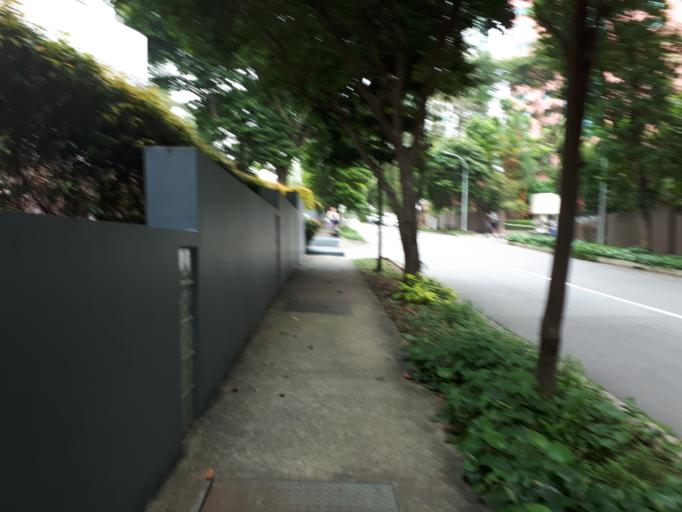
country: SG
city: Singapore
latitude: 1.2972
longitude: 103.8322
